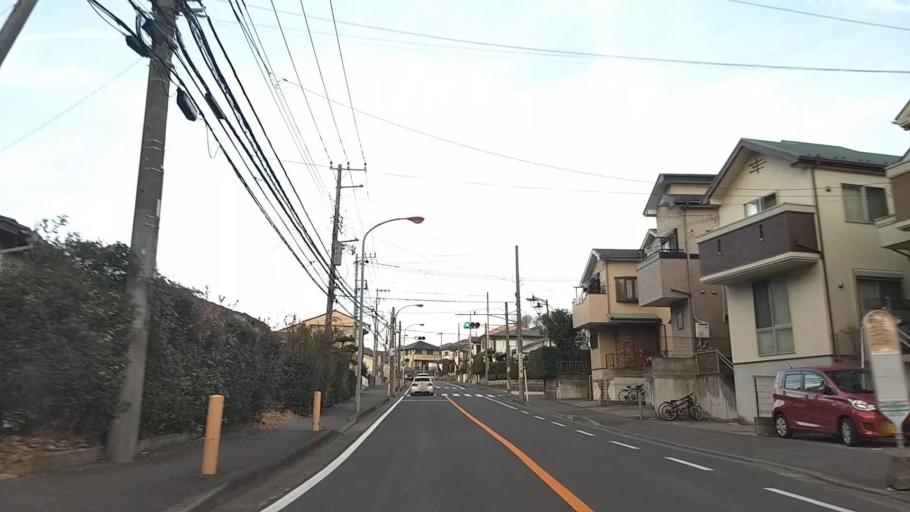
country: JP
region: Kanagawa
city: Atsugi
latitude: 35.4350
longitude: 139.3246
